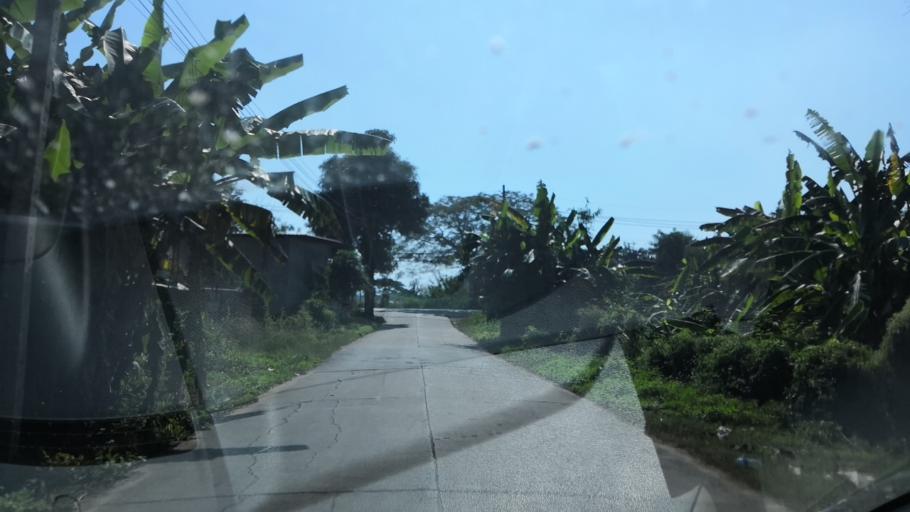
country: TH
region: Chiang Rai
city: Wiang Chai
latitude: 19.8802
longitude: 99.9417
